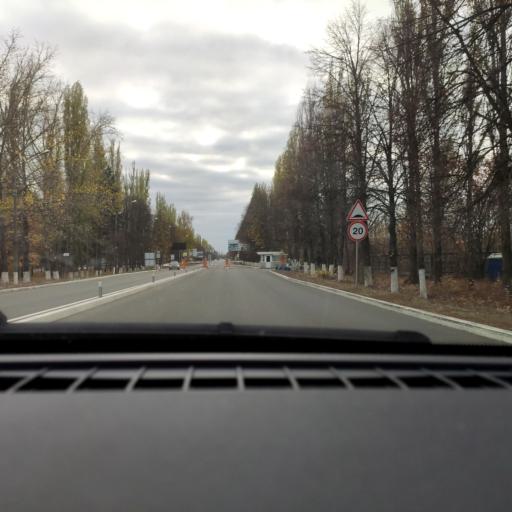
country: RU
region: Voronezj
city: Podgornoye
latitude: 51.8111
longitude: 39.2232
